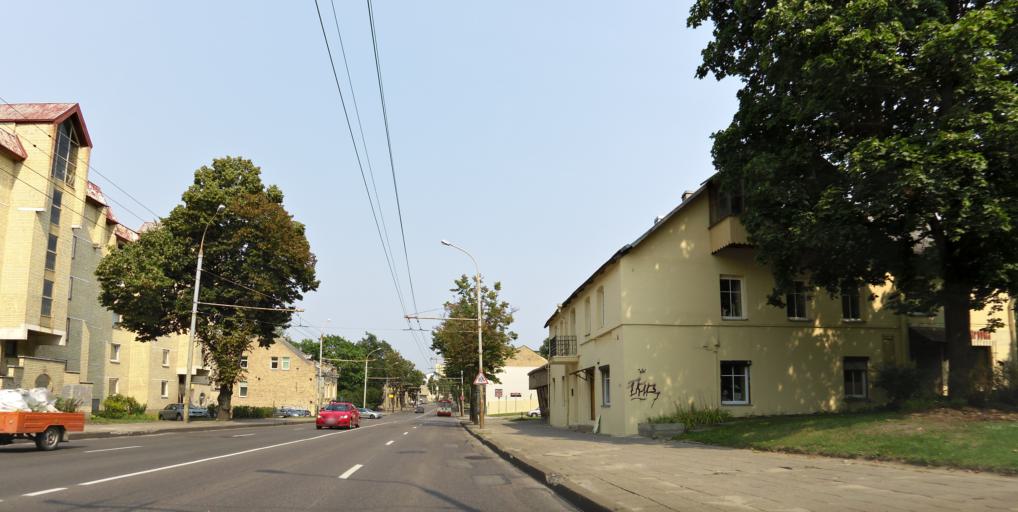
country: LT
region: Vilnius County
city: Rasos
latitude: 54.6998
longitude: 25.3090
